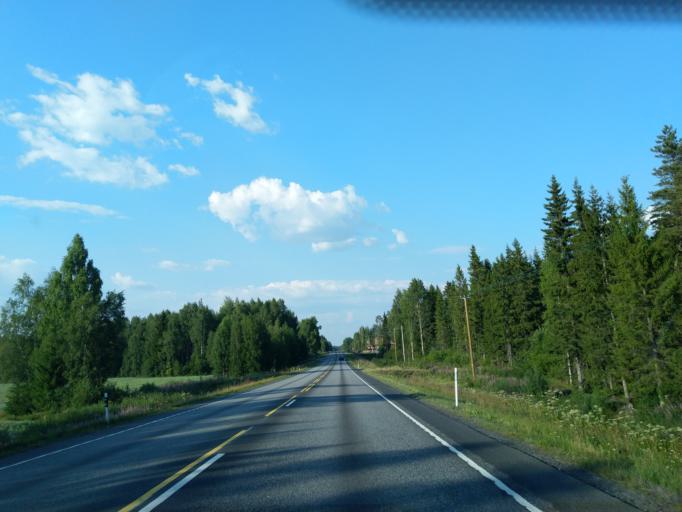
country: FI
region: Satakunta
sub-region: Pori
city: Pomarkku
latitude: 61.7259
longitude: 22.0631
